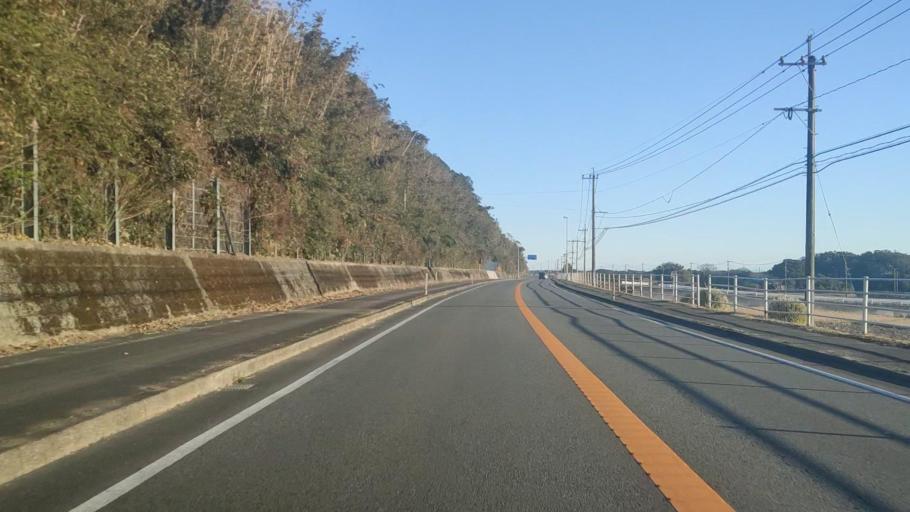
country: JP
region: Miyazaki
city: Takanabe
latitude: 32.1048
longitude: 131.5227
